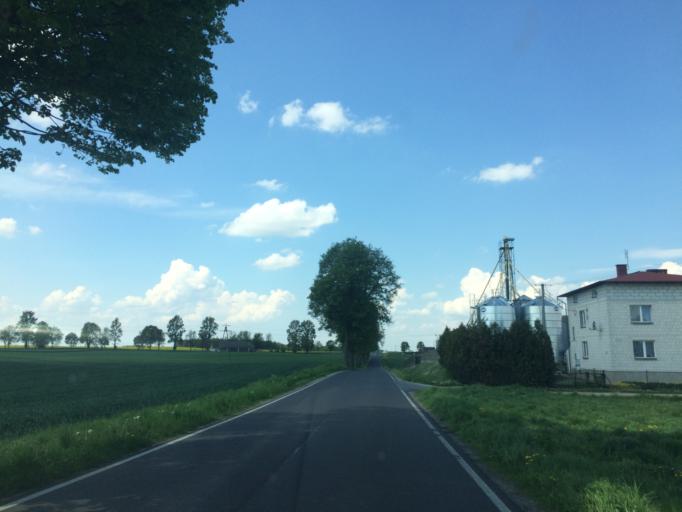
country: PL
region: Warmian-Masurian Voivodeship
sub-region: Powiat ilawski
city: Lubawa
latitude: 53.4071
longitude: 19.8046
